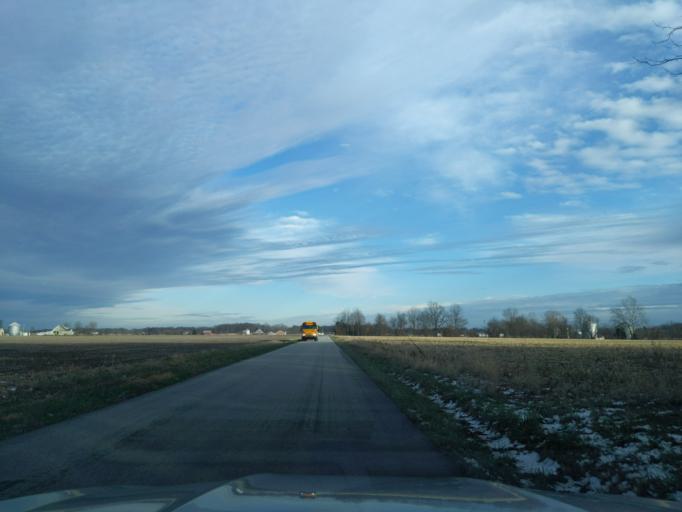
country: US
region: Indiana
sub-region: Decatur County
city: Westport
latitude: 39.2192
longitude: -85.4717
